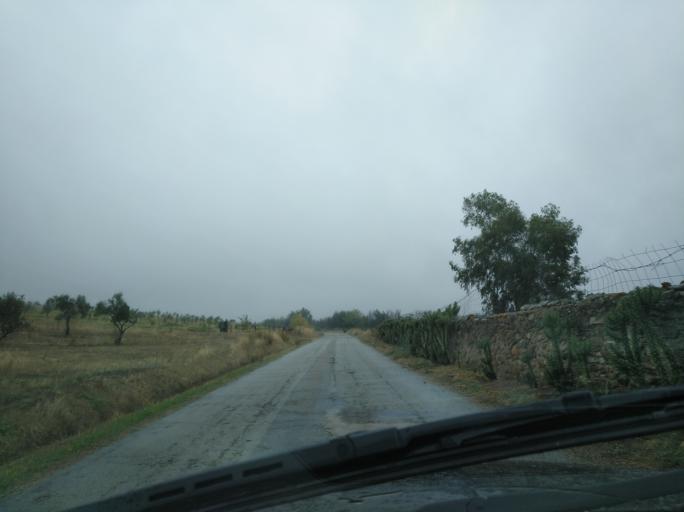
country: PT
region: Portalegre
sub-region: Campo Maior
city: Campo Maior
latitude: 38.9815
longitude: -7.0690
